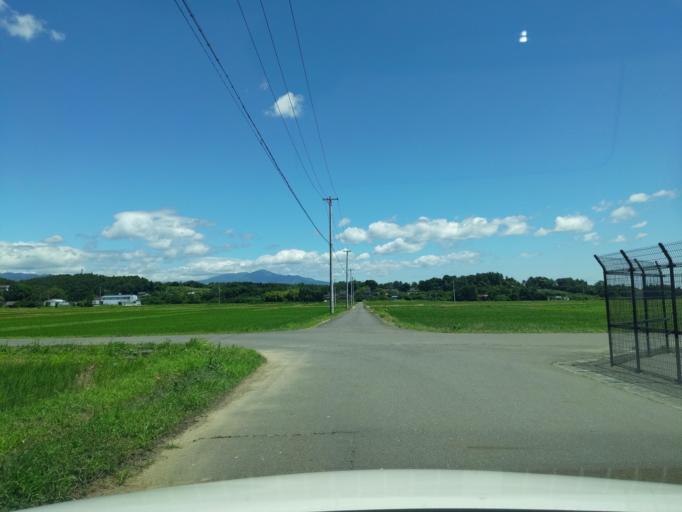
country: JP
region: Fukushima
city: Koriyama
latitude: 37.4009
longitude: 140.2748
